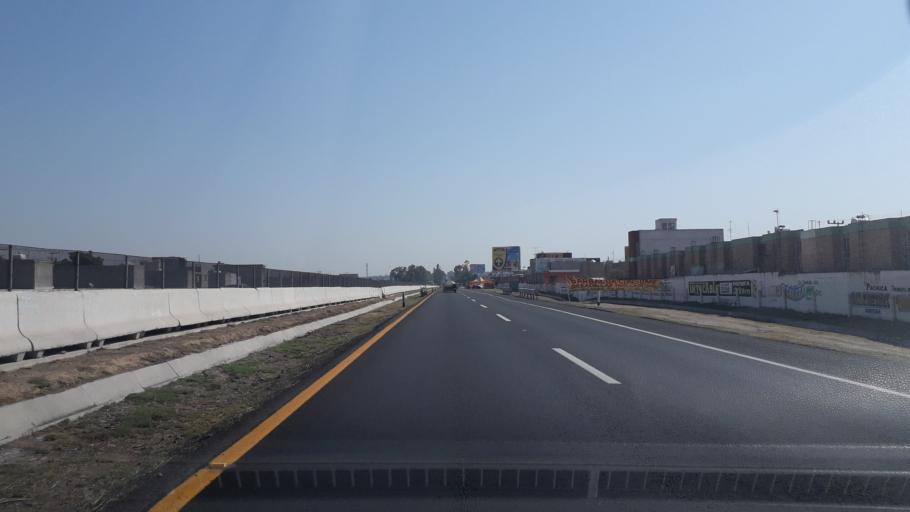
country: MX
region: Mexico
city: Santo Tomas Chiconautla
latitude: 19.6350
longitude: -99.0209
